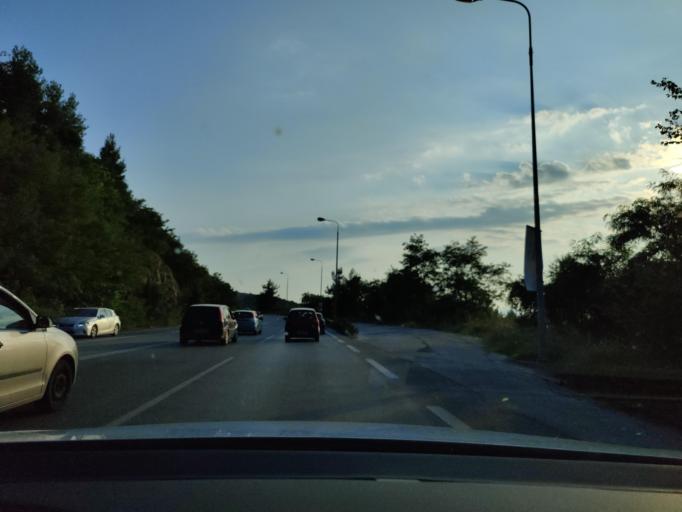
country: GR
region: East Macedonia and Thrace
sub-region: Nomos Kavalas
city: Amygdaleonas
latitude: 40.9504
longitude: 24.3715
